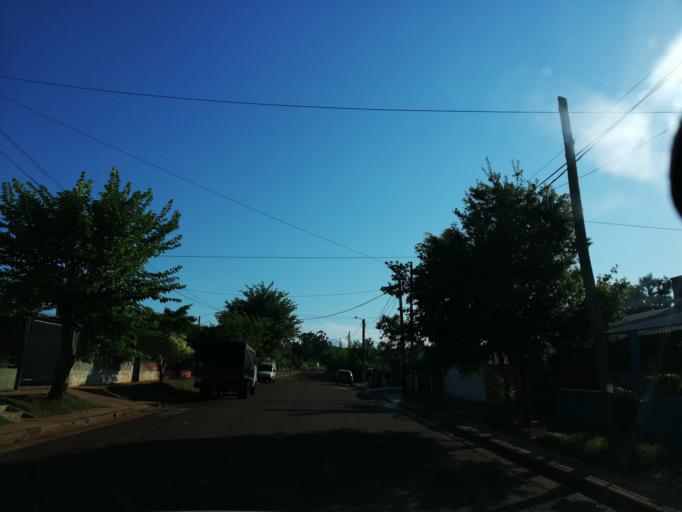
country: AR
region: Misiones
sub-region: Departamento de Capital
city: Posadas
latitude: -27.4337
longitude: -55.9448
